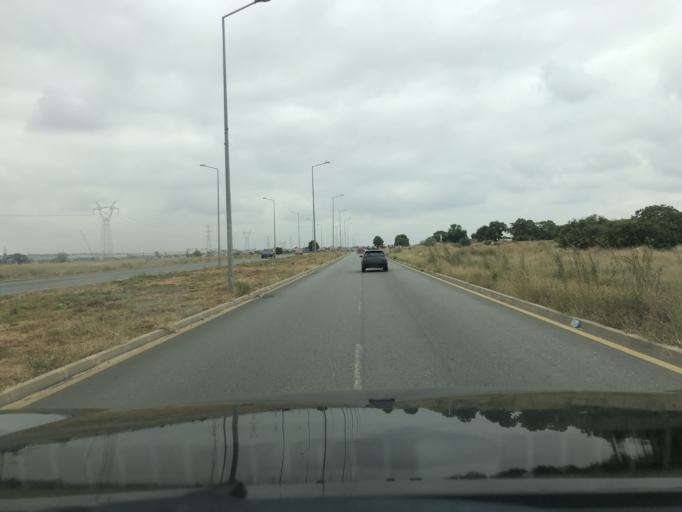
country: AO
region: Luanda
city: Luanda
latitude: -8.9758
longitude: 13.2788
